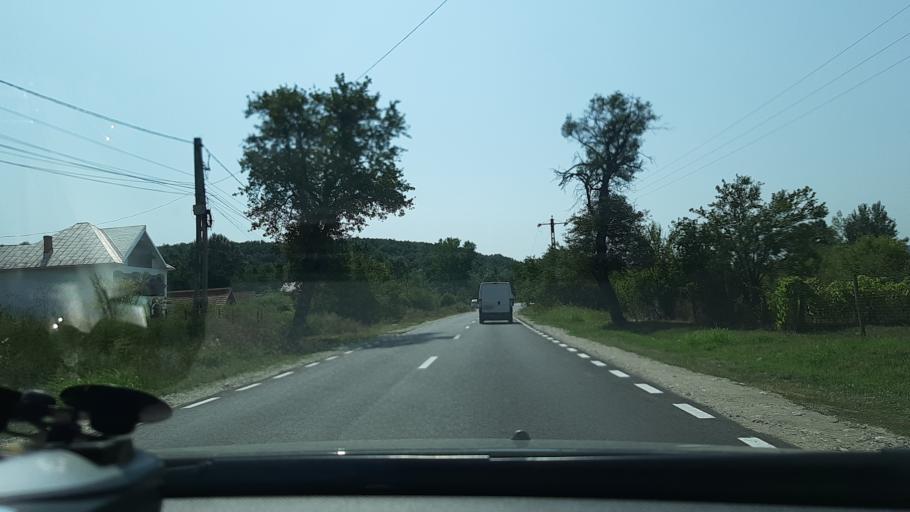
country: RO
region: Gorj
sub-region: Comuna Targu Carbunesti
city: Pojogeni
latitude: 44.9776
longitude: 23.5017
